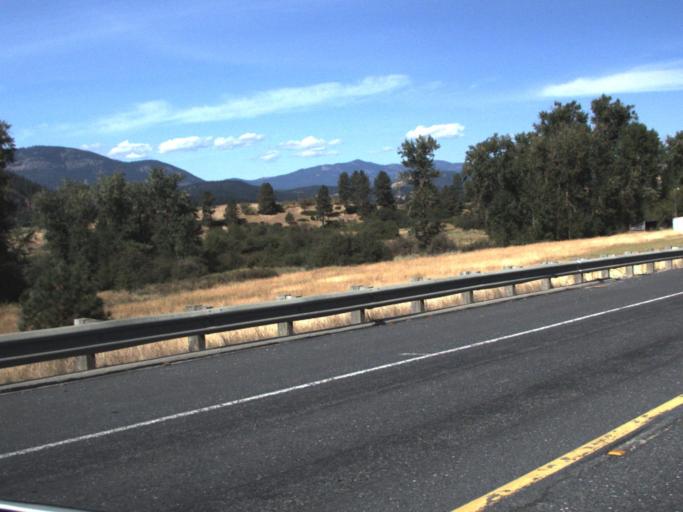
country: US
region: Washington
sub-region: Stevens County
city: Chewelah
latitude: 48.3287
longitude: -117.8271
